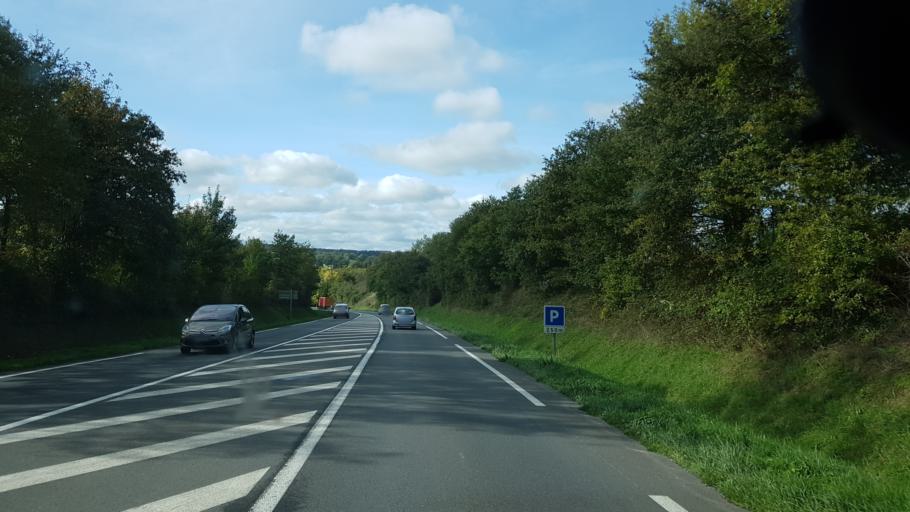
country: FR
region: Poitou-Charentes
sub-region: Departement de la Charente
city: Confolens
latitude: 46.0642
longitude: 0.6894
